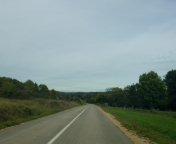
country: FR
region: Bourgogne
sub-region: Departement de Saone-et-Loire
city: Cuiseaux
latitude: 46.4525
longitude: 5.4255
